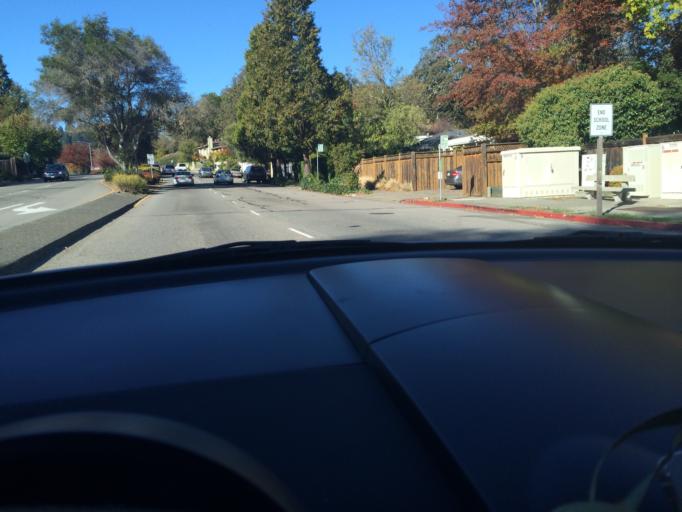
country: US
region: California
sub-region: Marin County
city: Kentfield
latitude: 37.9536
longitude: -122.5408
